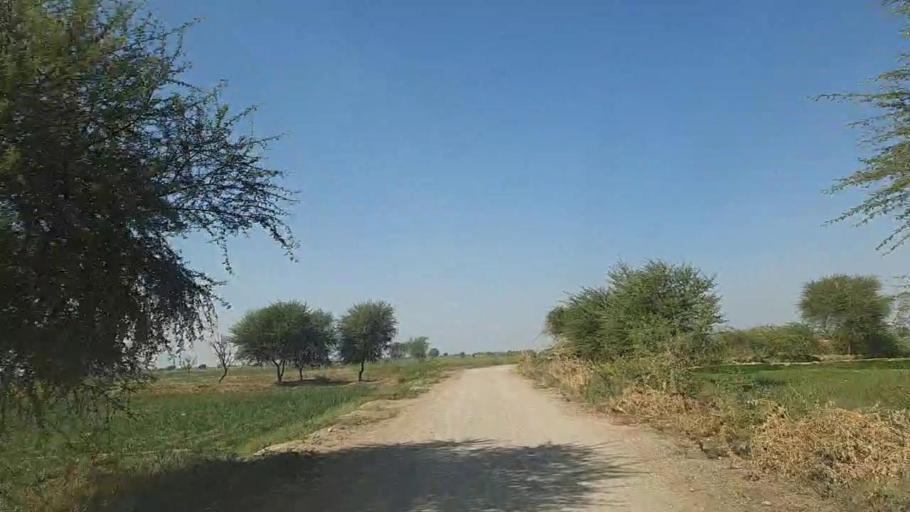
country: PK
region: Sindh
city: Naukot
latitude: 25.0173
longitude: 69.3593
